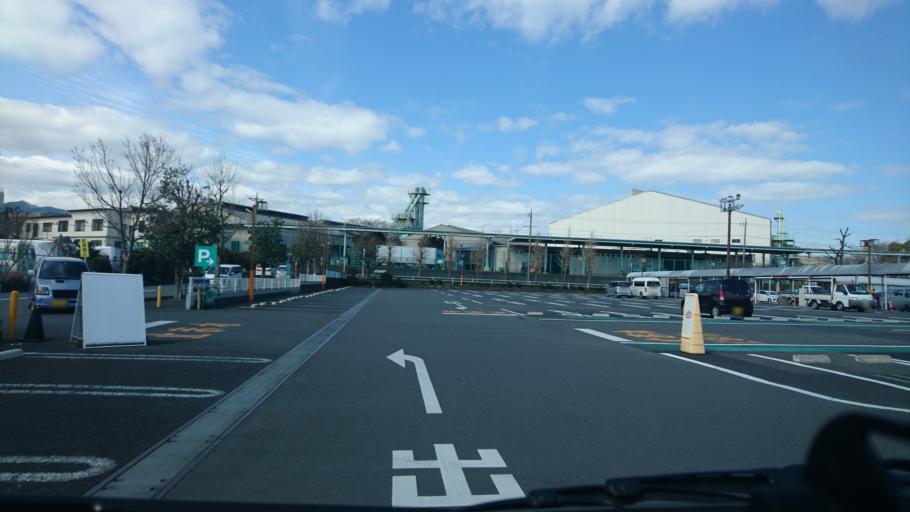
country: JP
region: Kanagawa
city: Zama
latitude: 35.5321
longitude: 139.3292
